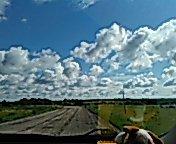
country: RU
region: Penza
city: Mokshan
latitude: 53.3815
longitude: 44.2606
